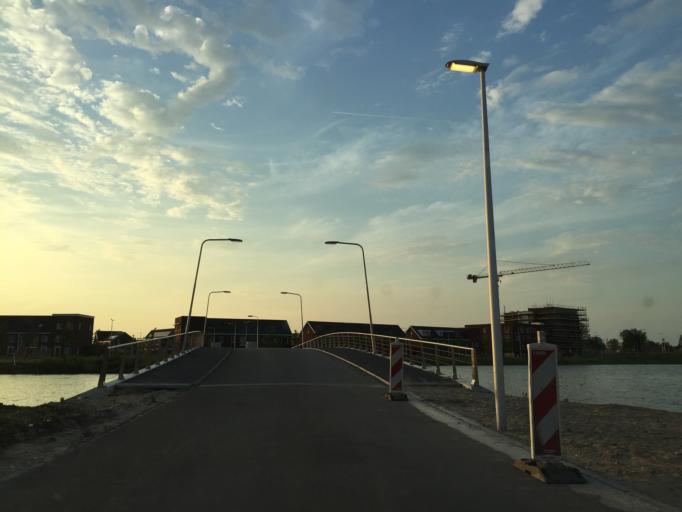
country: NL
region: South Holland
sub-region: Gemeente Gouda
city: Bloemendaal
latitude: 52.0020
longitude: 4.6833
